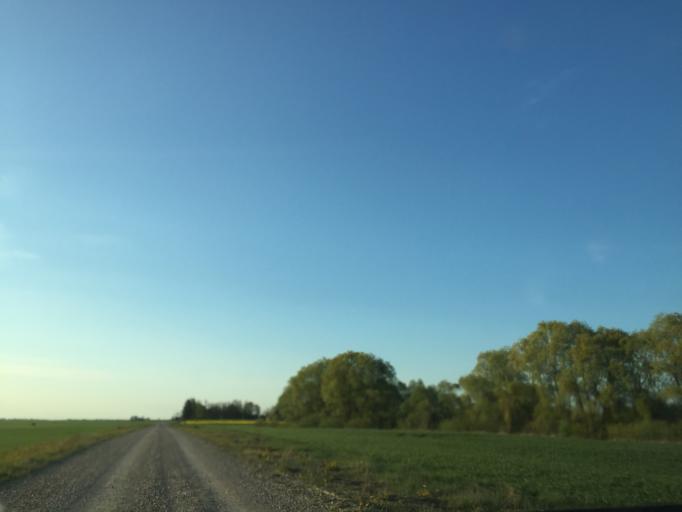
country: LV
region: Bauskas Rajons
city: Bauska
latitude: 56.2992
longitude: 24.1798
